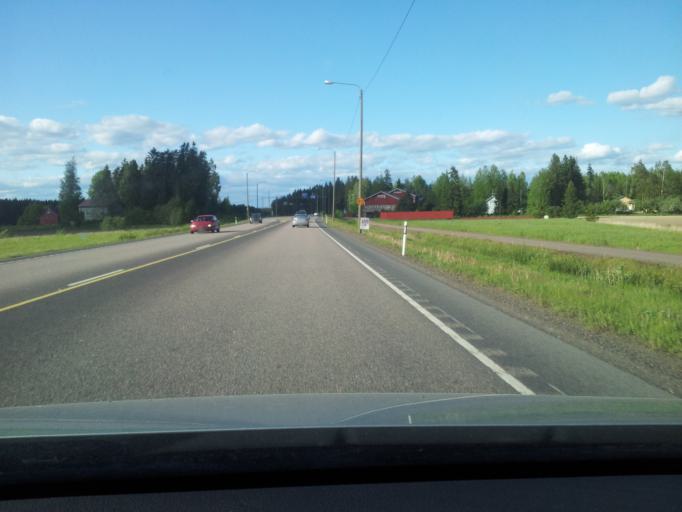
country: FI
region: Kymenlaakso
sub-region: Kouvola
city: Elimaeki
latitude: 60.8241
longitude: 26.5345
